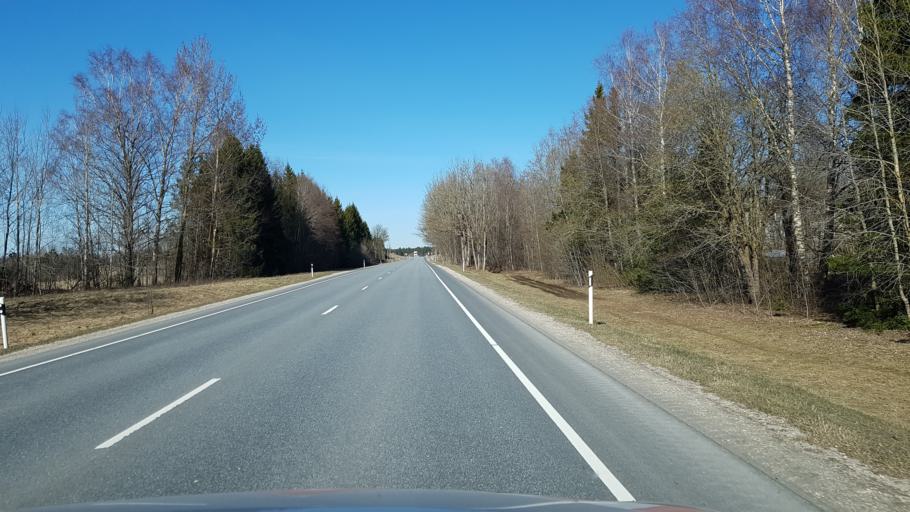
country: EE
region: Harju
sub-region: Nissi vald
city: Turba
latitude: 59.0445
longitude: 24.1717
